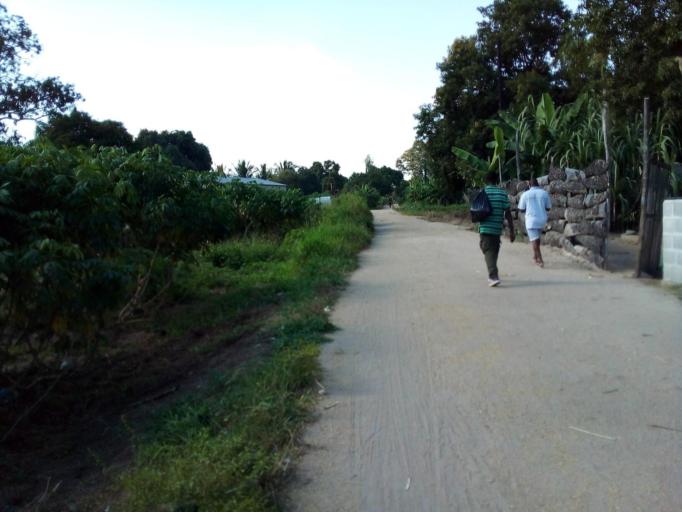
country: MZ
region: Zambezia
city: Quelimane
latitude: -17.6031
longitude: 36.8221
